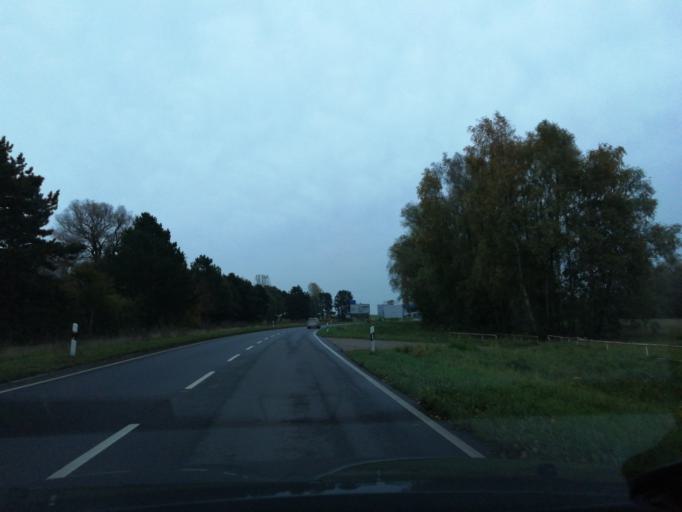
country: DE
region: Lower Saxony
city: Wilhelmshaven
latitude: 53.5815
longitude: 8.1249
